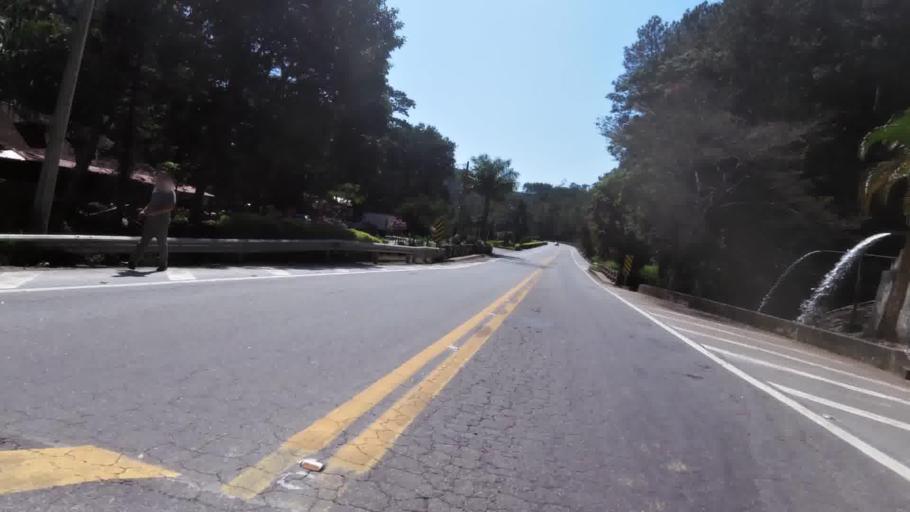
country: BR
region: Espirito Santo
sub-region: Marechal Floriano
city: Marechal Floriano
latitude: -20.4162
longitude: -40.8629
